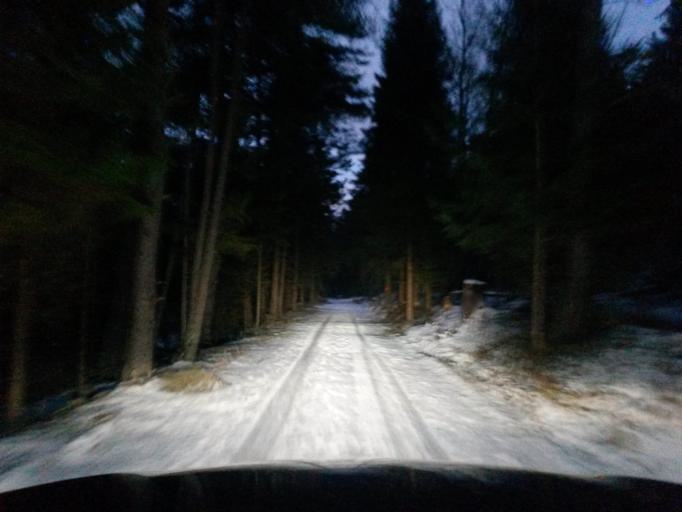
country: SK
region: Kosicky
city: Medzev
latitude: 48.7892
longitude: 20.8045
